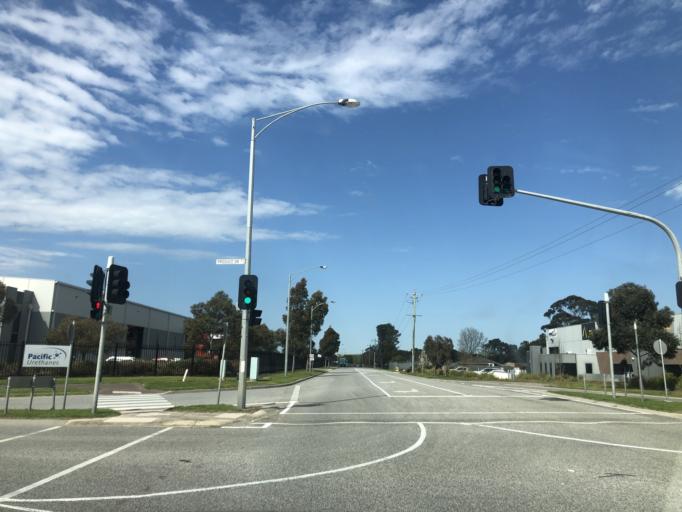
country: AU
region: Victoria
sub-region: Casey
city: Hampton Park
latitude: -38.0402
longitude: 145.2186
